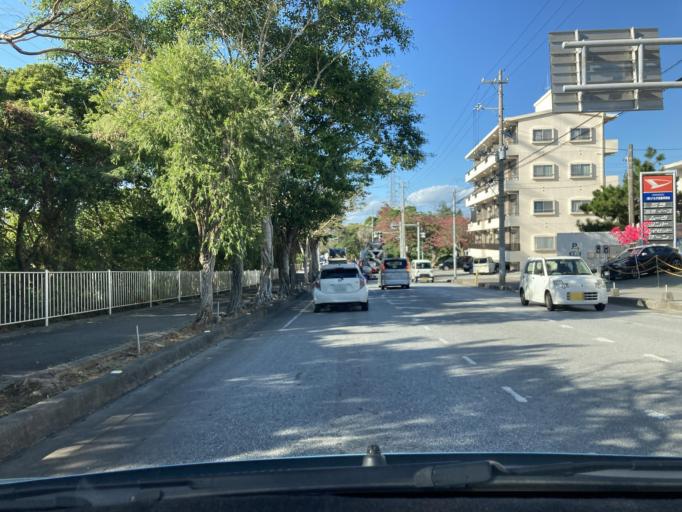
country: JP
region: Okinawa
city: Gushikawa
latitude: 26.3625
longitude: 127.8432
